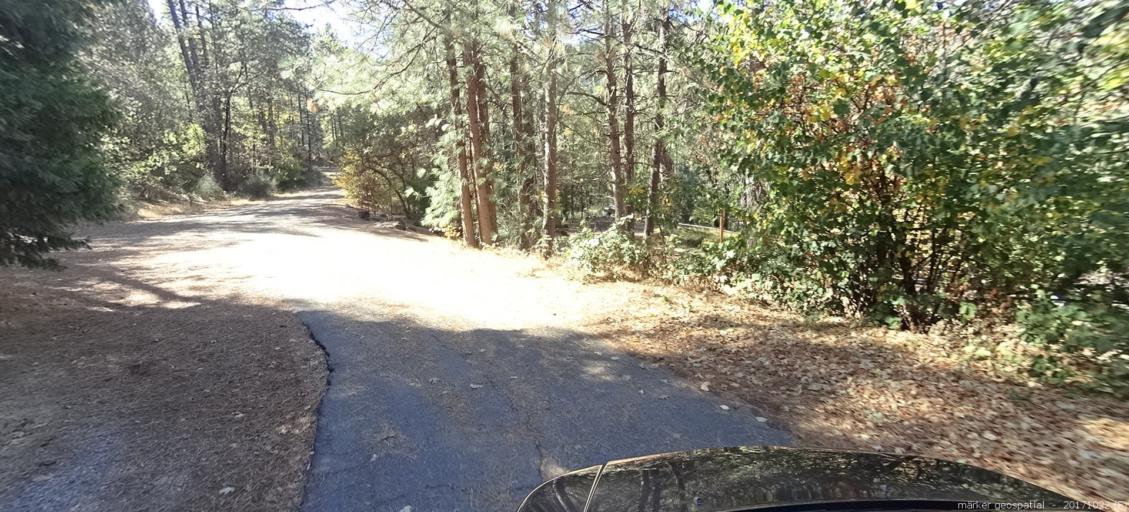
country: US
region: California
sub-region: Shasta County
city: Central Valley (historical)
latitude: 40.9231
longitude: -122.4031
